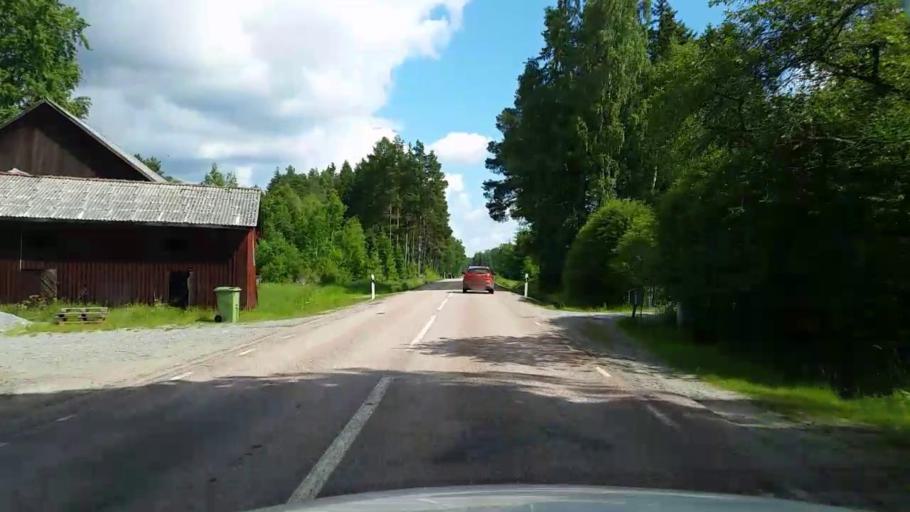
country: SE
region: Vaestmanland
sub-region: Skinnskattebergs Kommun
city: Skinnskatteberg
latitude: 59.7533
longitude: 15.8148
